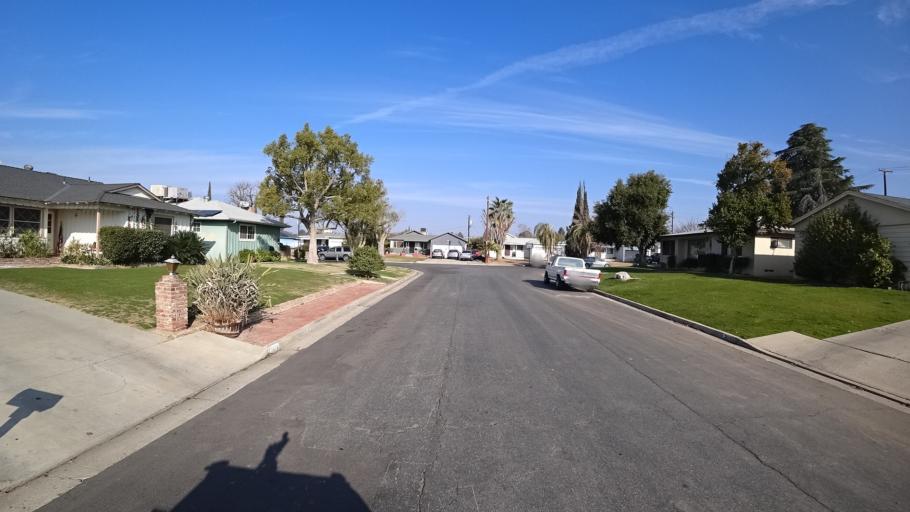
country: US
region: California
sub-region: Kern County
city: Oildale
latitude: 35.4009
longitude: -118.9775
